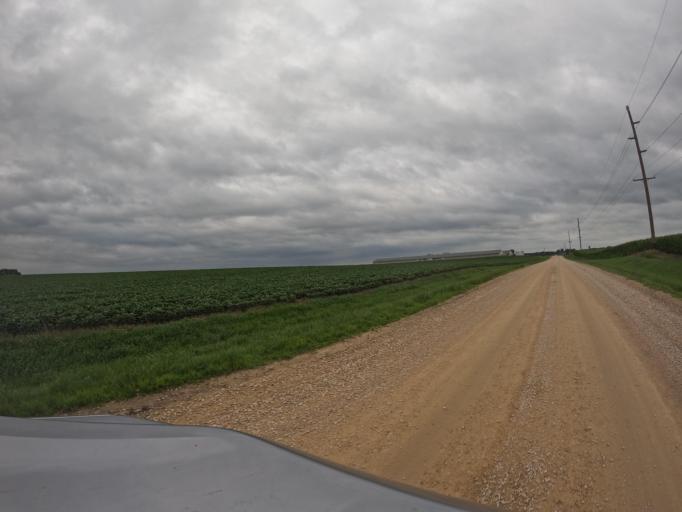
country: US
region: Iowa
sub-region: Clinton County
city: De Witt
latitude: 41.7966
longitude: -90.4714
